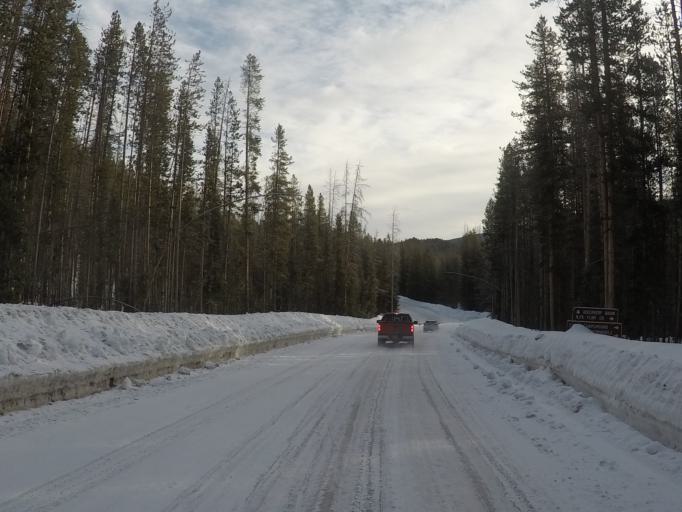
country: US
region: Montana
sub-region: Granite County
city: Philipsburg
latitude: 46.2235
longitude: -113.2528
